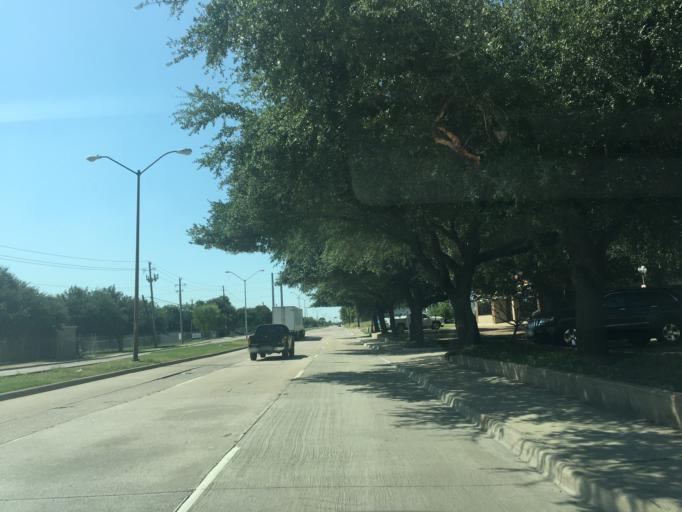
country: US
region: Texas
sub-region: Dallas County
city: Garland
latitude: 32.8606
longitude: -96.6659
